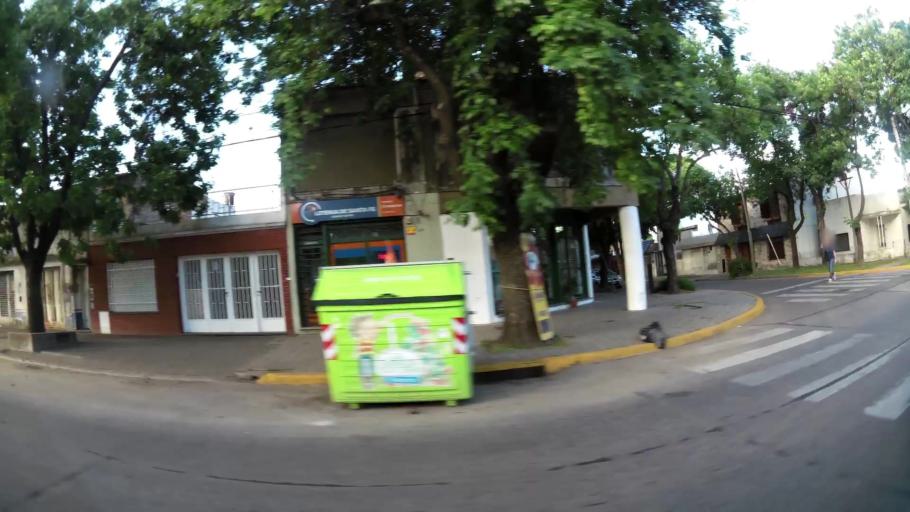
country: AR
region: Santa Fe
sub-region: Departamento de Rosario
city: Rosario
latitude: -32.9758
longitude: -60.6644
